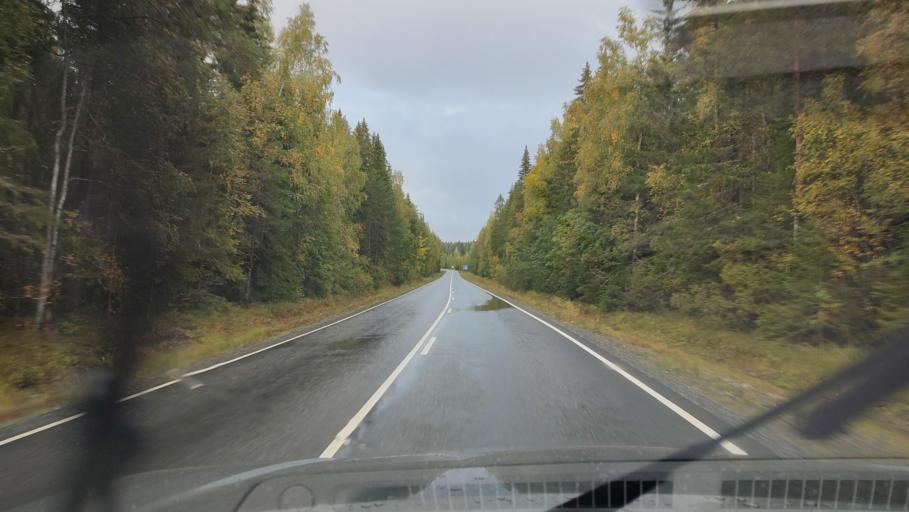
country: FI
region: Southern Ostrobothnia
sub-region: Suupohja
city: Karijoki
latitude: 62.2806
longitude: 21.6154
